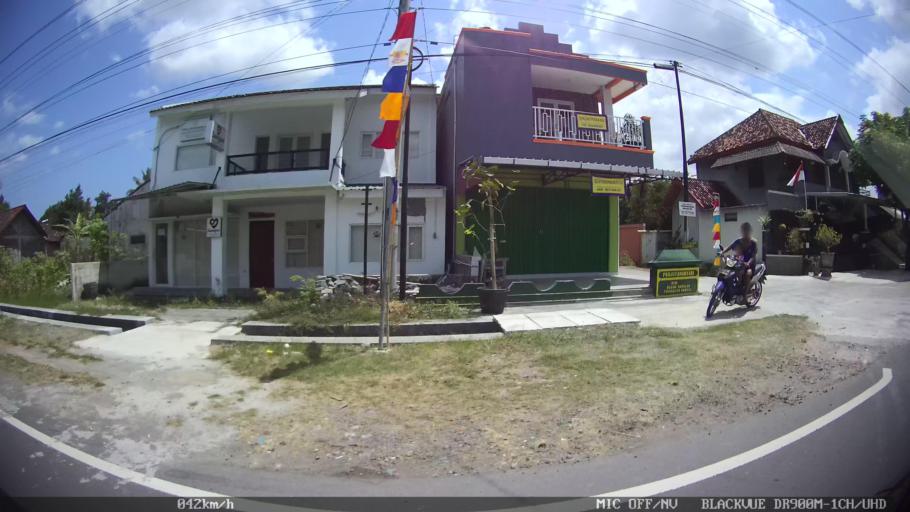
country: ID
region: Daerah Istimewa Yogyakarta
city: Bantul
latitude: -7.9053
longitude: 110.3451
